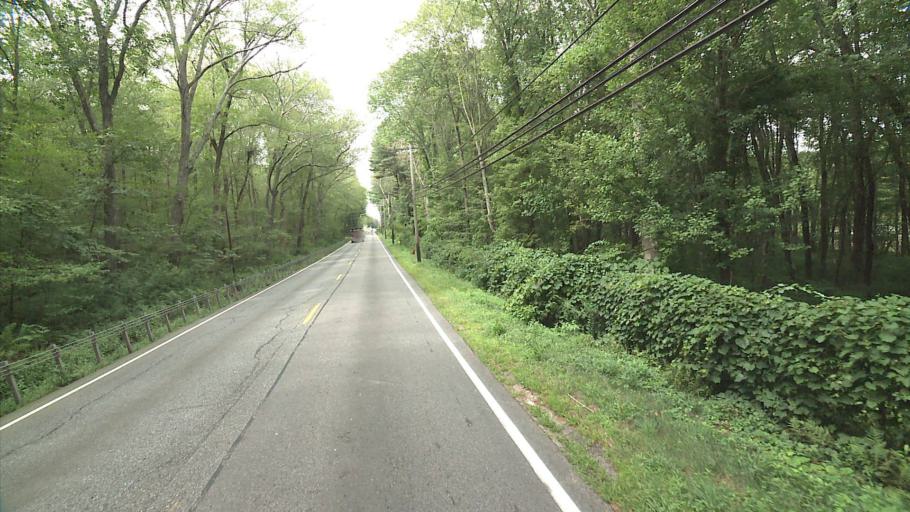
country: US
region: Connecticut
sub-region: New London County
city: Montville Center
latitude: 41.4191
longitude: -72.1955
